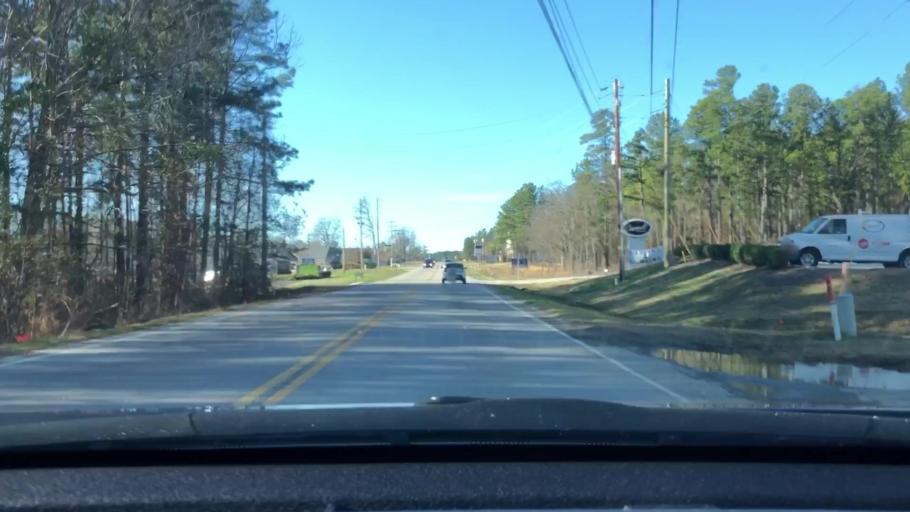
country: US
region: South Carolina
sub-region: Lexington County
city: Irmo
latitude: 34.1128
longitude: -81.1936
